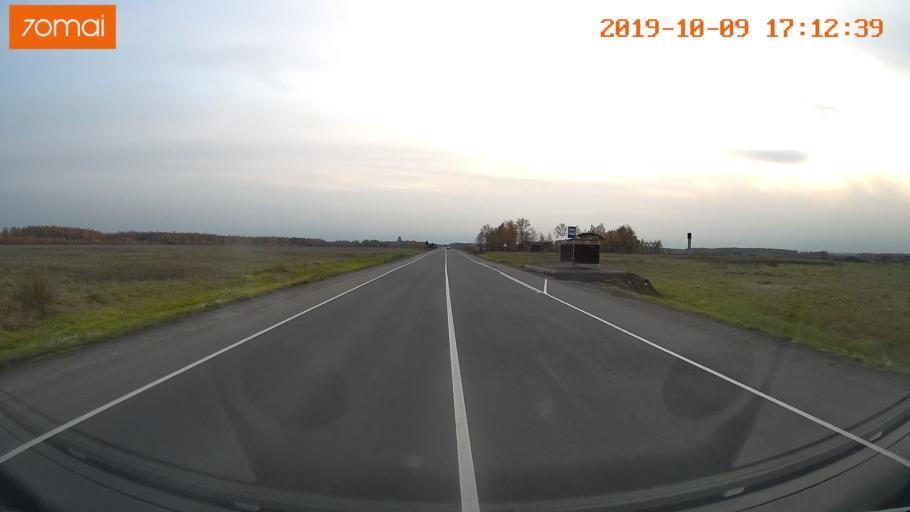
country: RU
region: Ivanovo
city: Privolzhsk
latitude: 57.3260
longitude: 41.2386
